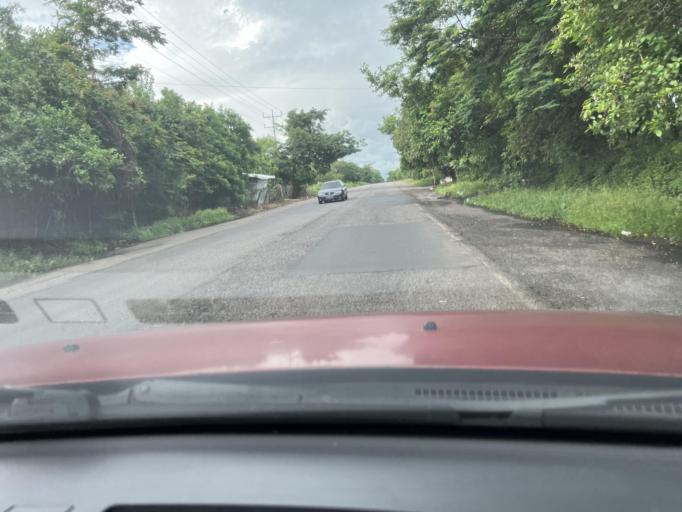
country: SV
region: La Union
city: San Alejo
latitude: 13.4132
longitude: -87.8896
